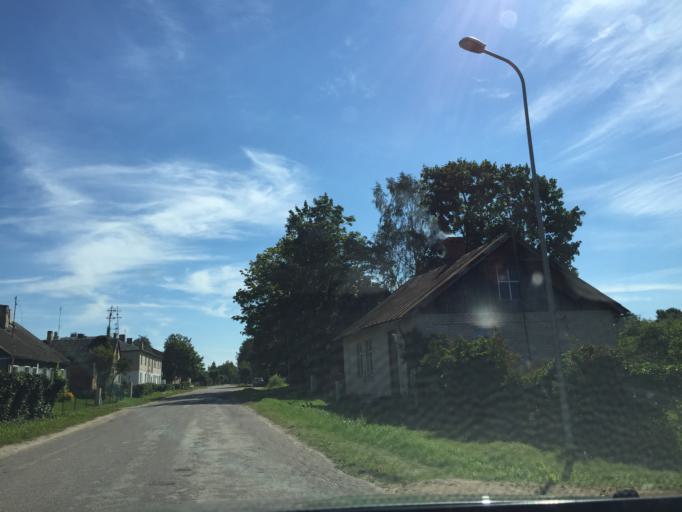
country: LV
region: Plavinu
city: Plavinas
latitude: 56.6136
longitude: 25.7712
